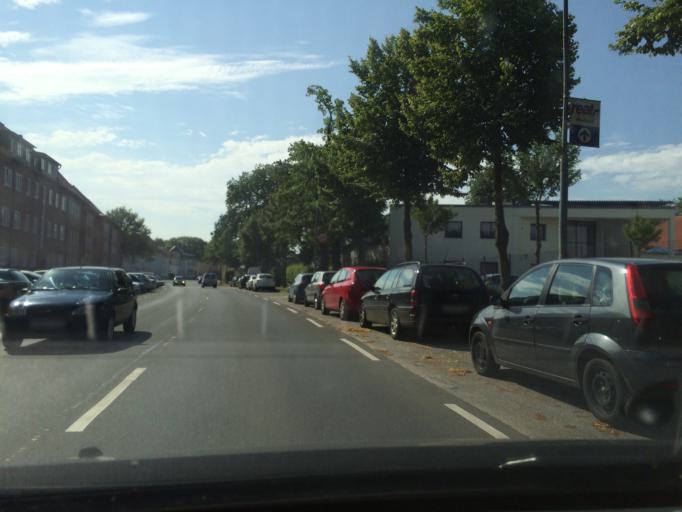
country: DE
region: Mecklenburg-Vorpommern
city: Stralsund
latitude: 54.3063
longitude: 13.0899
